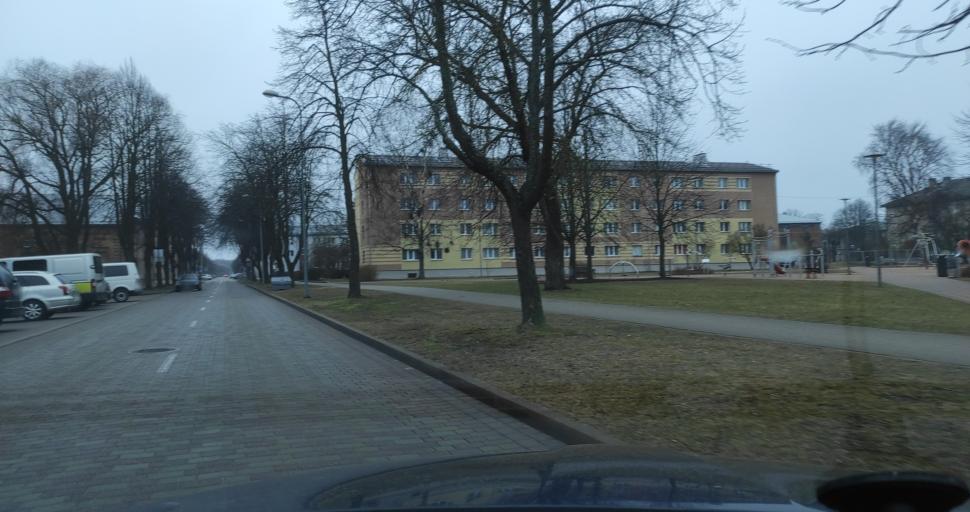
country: LV
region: Ventspils
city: Ventspils
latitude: 57.3885
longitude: 21.5609
